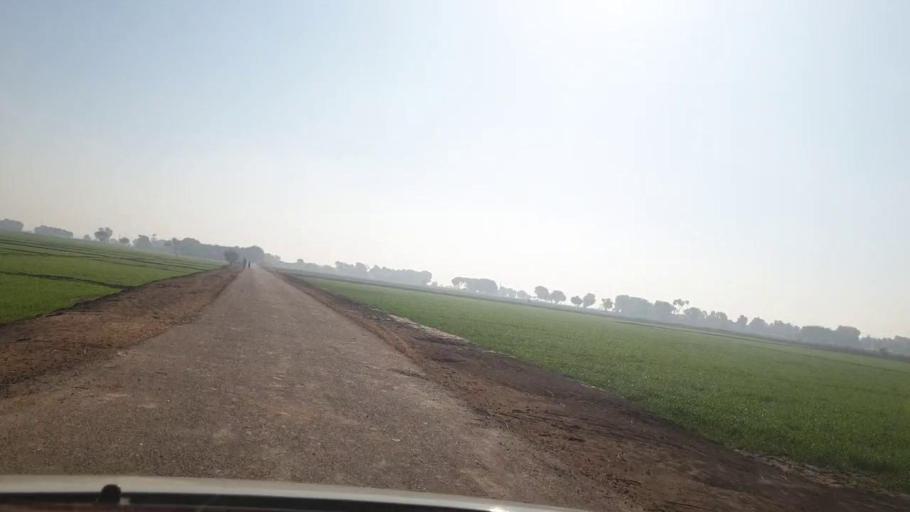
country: PK
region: Sindh
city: Dadu
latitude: 26.6390
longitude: 67.8308
